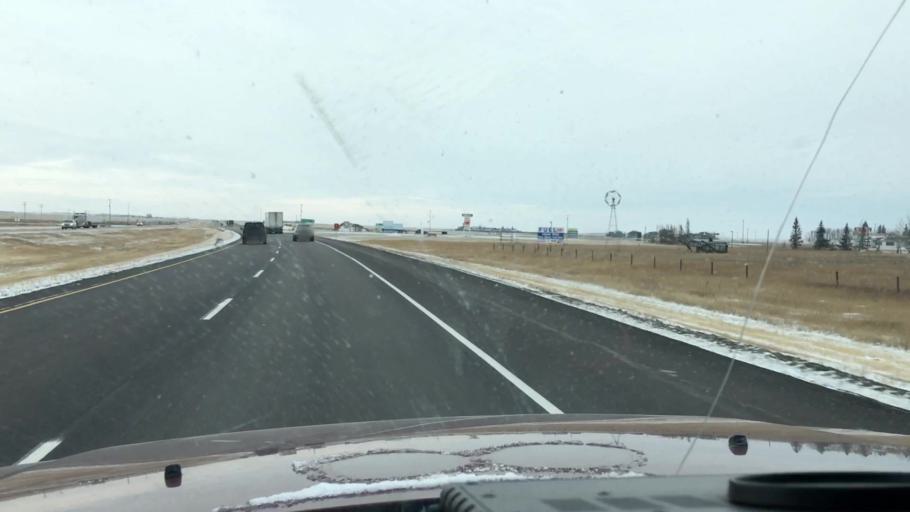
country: CA
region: Saskatchewan
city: Saskatoon
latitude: 51.8127
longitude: -106.4973
